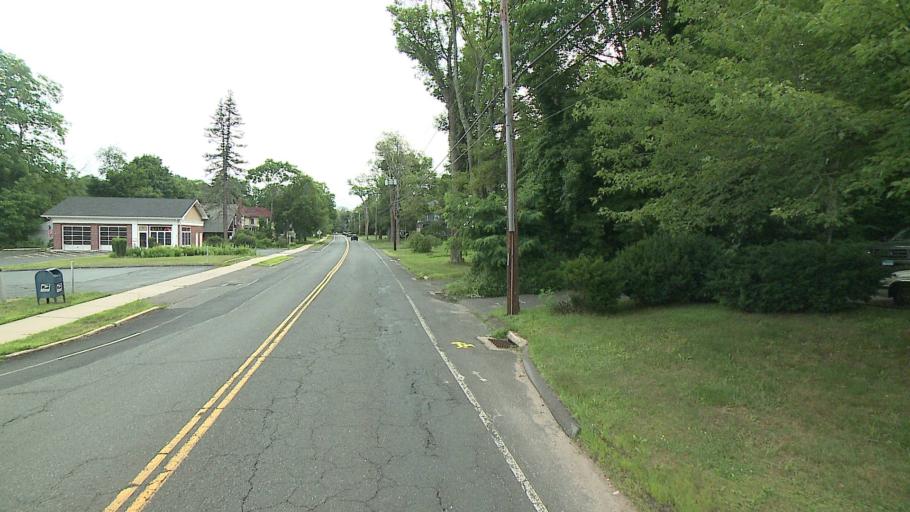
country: US
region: Connecticut
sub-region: Hartford County
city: Collinsville
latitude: 41.8140
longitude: -72.9194
